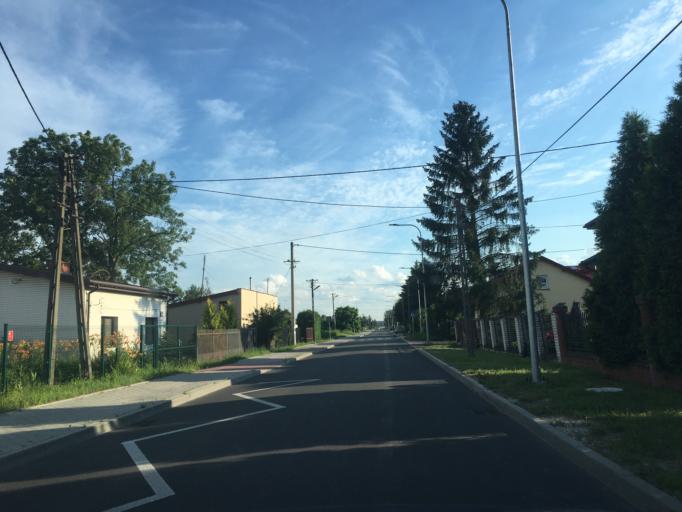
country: PL
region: Masovian Voivodeship
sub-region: Powiat wolominski
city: Radzymin
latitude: 52.4053
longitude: 21.2094
